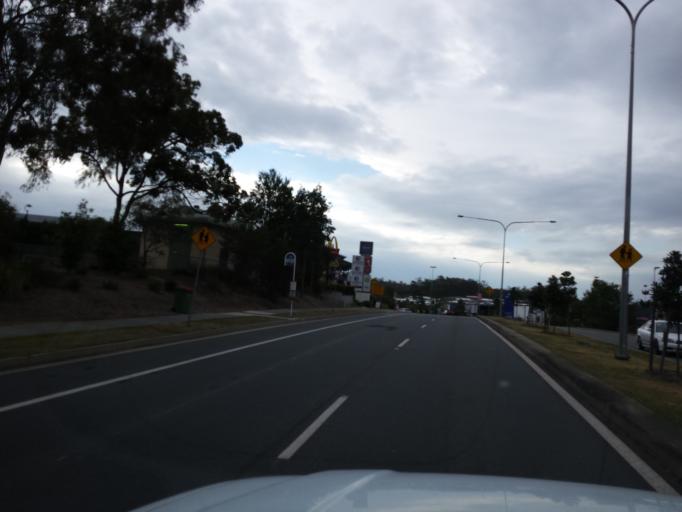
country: AU
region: Queensland
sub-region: Gold Coast
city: Oxenford
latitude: -27.8535
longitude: 153.3009
